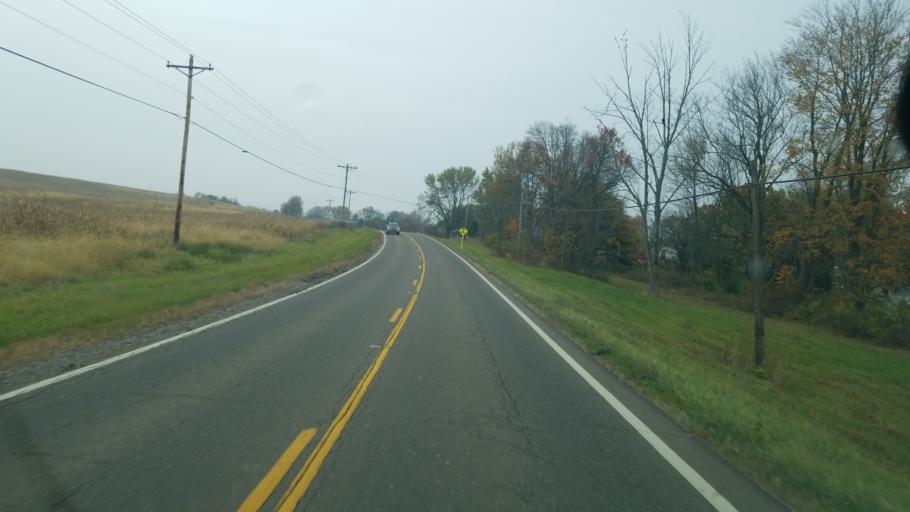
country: US
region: Ohio
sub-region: Holmes County
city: Millersburg
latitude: 40.4719
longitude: -81.9018
